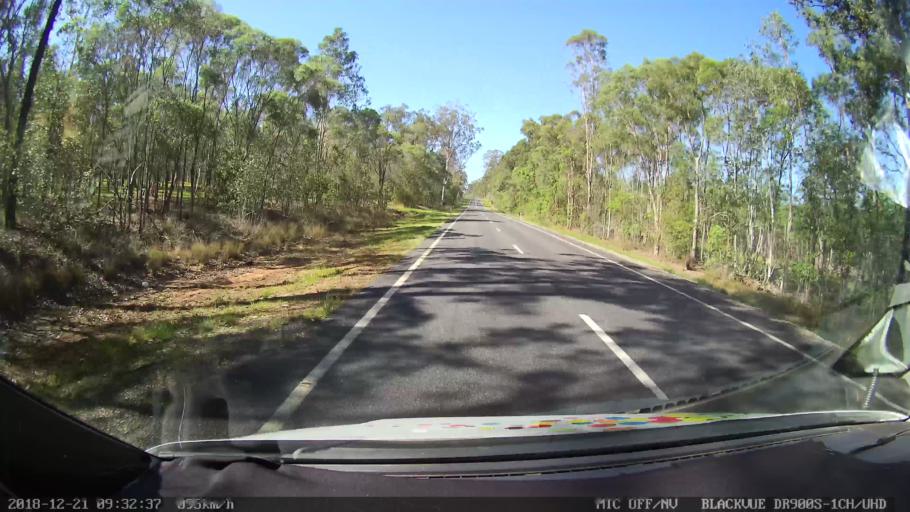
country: AU
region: New South Wales
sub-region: Clarence Valley
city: Maclean
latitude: -29.4729
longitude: 152.9778
